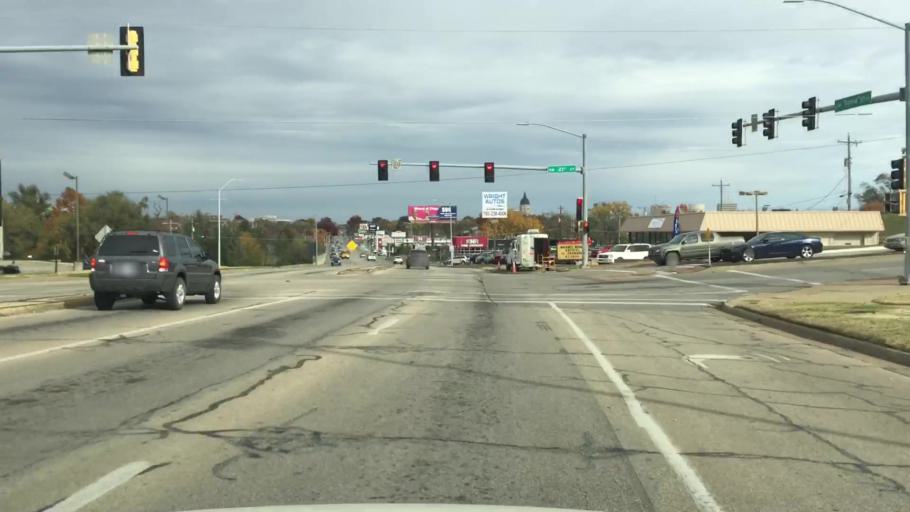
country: US
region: Kansas
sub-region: Shawnee County
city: Topeka
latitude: 39.0294
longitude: -95.6829
